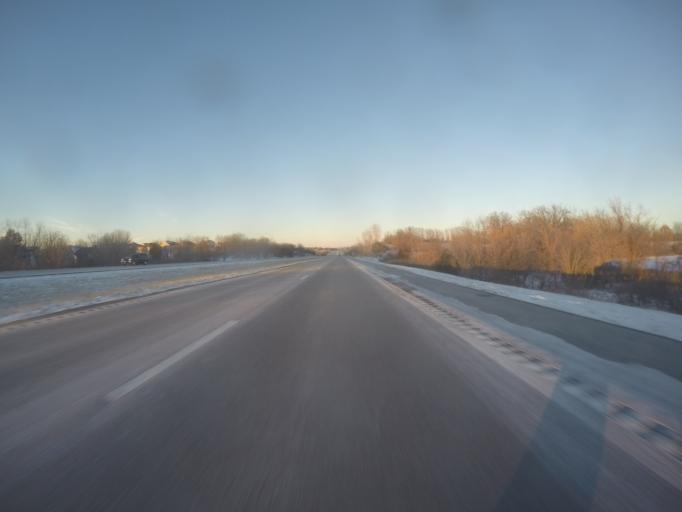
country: US
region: Missouri
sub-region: Platte County
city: Platte City
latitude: 39.3231
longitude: -94.7554
